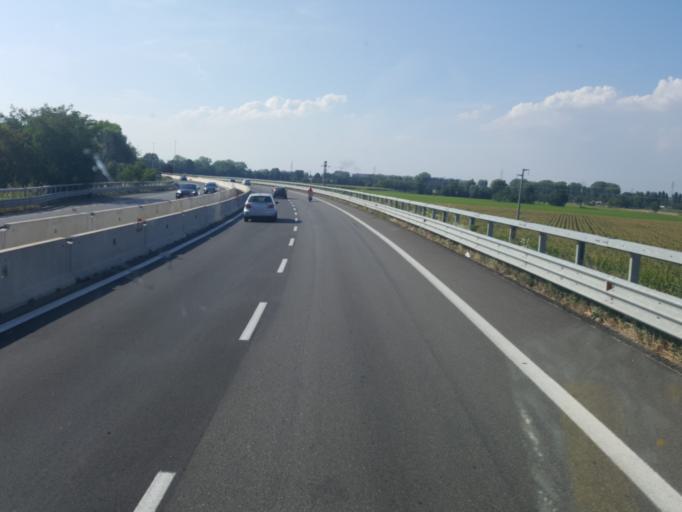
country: IT
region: Lombardy
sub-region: Citta metropolitana di Milano
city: Opera
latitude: 45.3791
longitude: 9.2263
